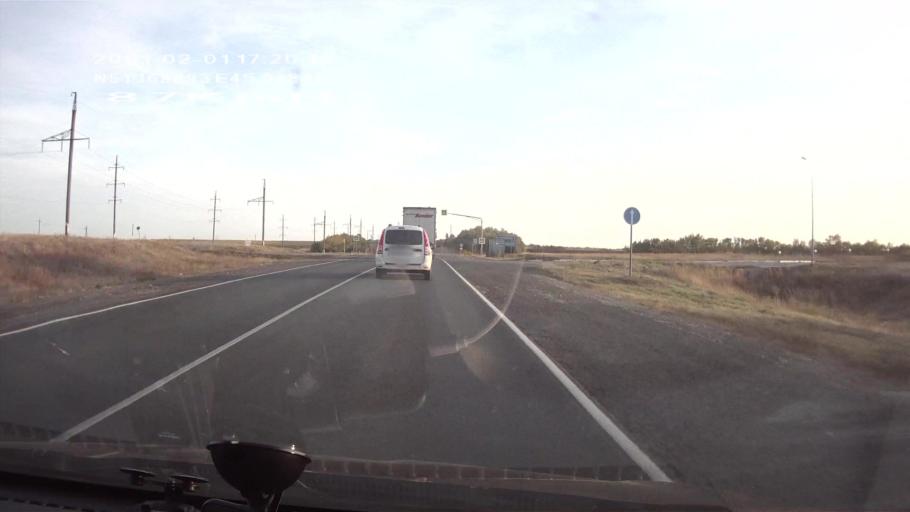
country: RU
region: Saratov
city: Krasnoarmeysk
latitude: 51.1678
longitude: 45.6489
